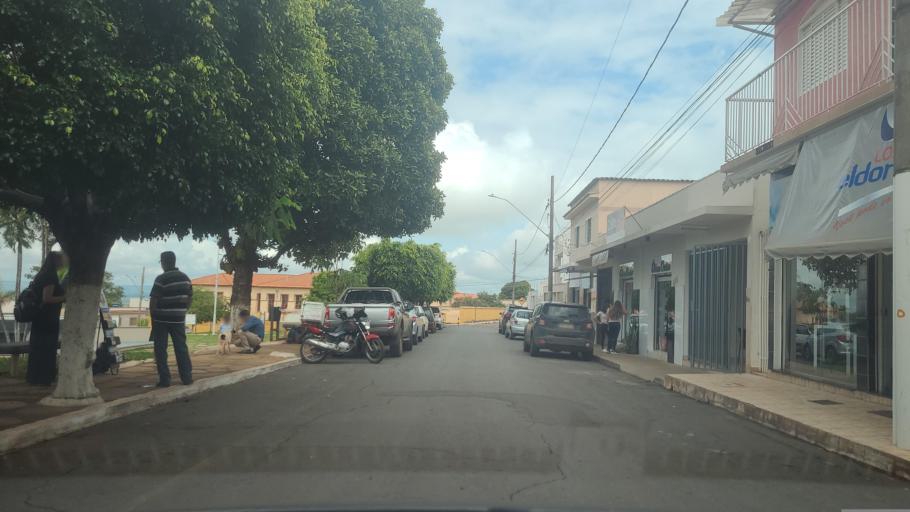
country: BR
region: Minas Gerais
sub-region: Carmo Do Paranaiba
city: Carmo do Paranaiba
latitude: -19.1937
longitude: -46.2467
